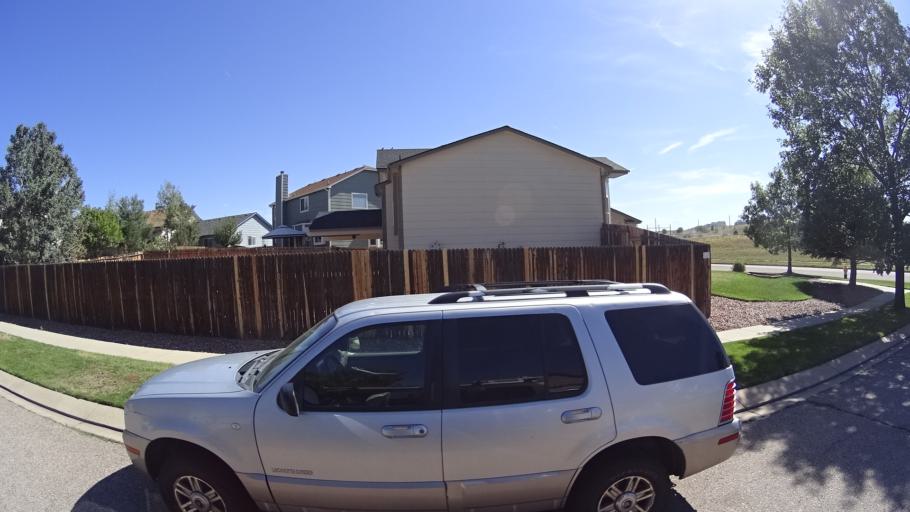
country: US
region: Colorado
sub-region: El Paso County
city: Black Forest
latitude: 38.9470
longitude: -104.7255
